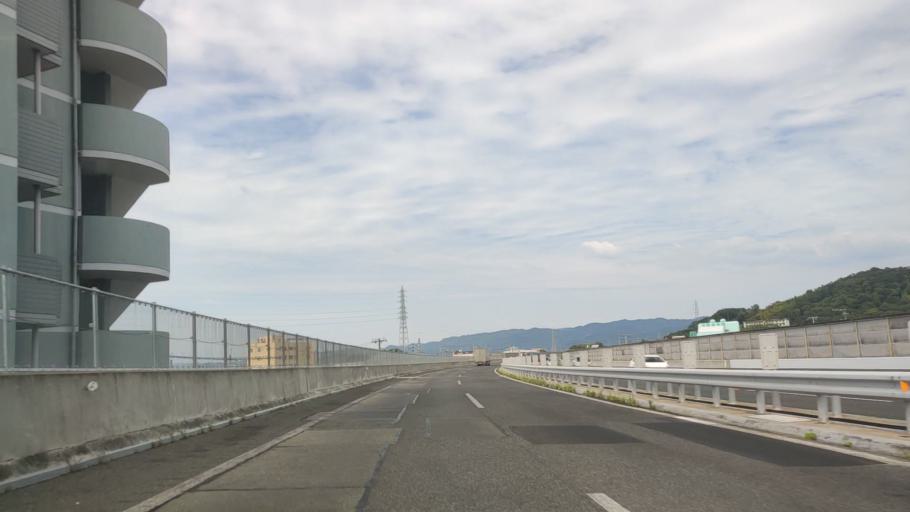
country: JP
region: Wakayama
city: Wakayama-shi
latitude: 34.2243
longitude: 135.2150
